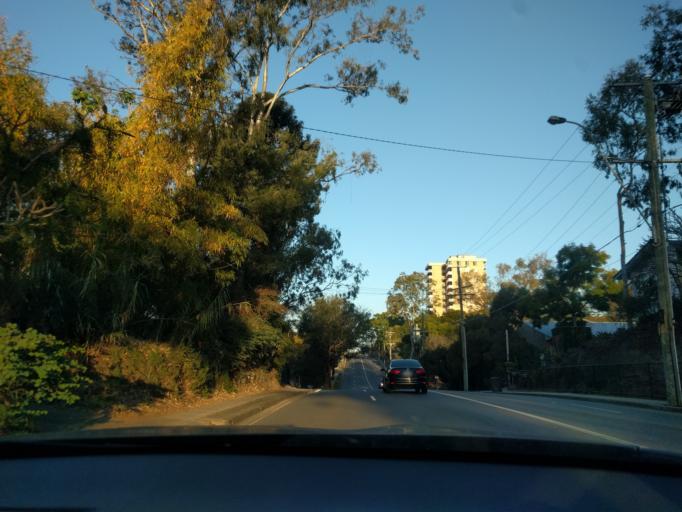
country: AU
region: Queensland
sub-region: Brisbane
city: Toowong
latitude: -27.4924
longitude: 152.9950
